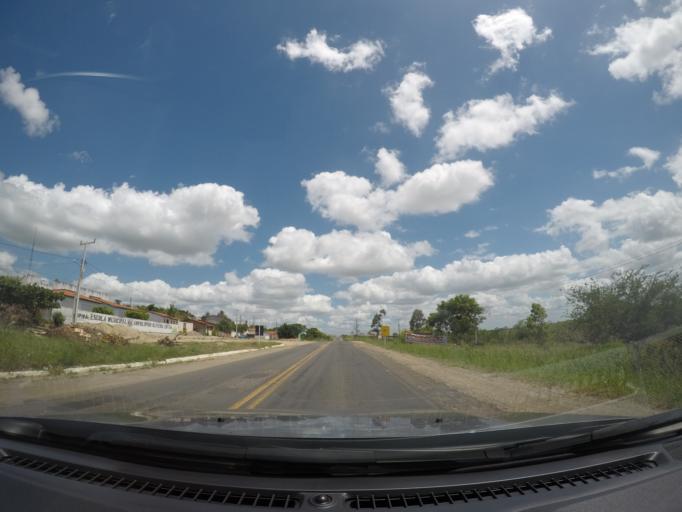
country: BR
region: Bahia
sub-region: Ipira
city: Ipira
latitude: -12.1837
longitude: -39.7094
